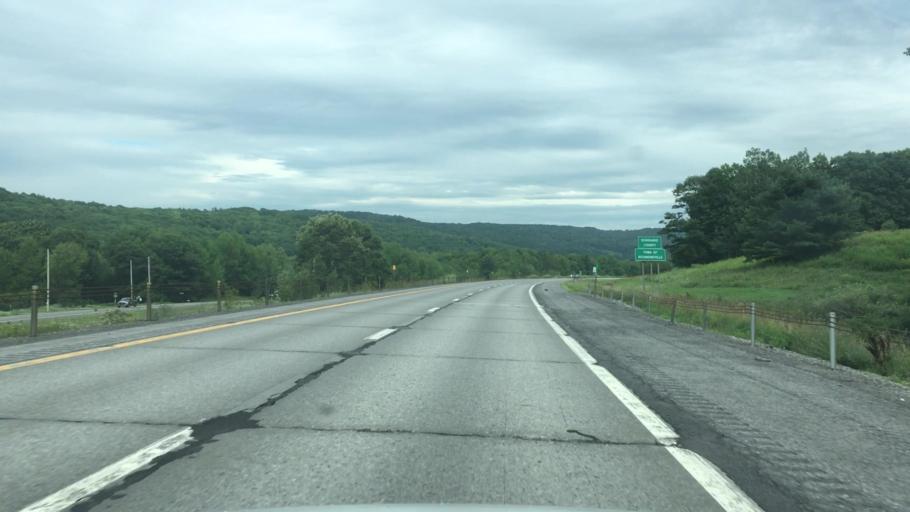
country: US
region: New York
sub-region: Otsego County
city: Worcester
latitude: 42.6491
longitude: -74.6354
